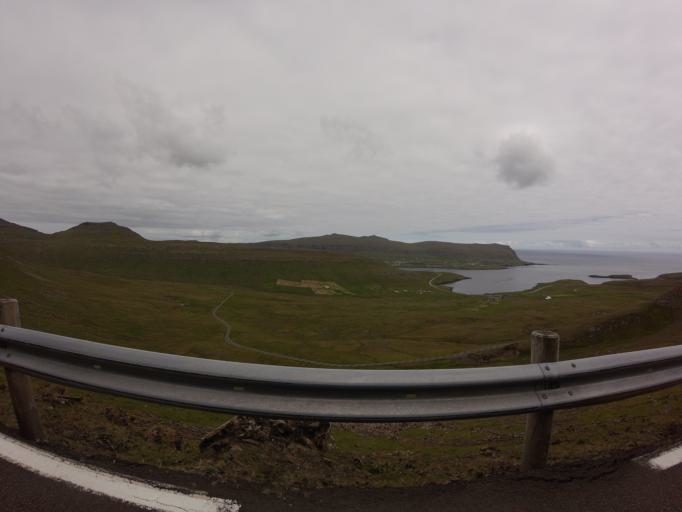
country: FO
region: Suduroy
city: Tvoroyri
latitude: 61.5246
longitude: -6.8362
